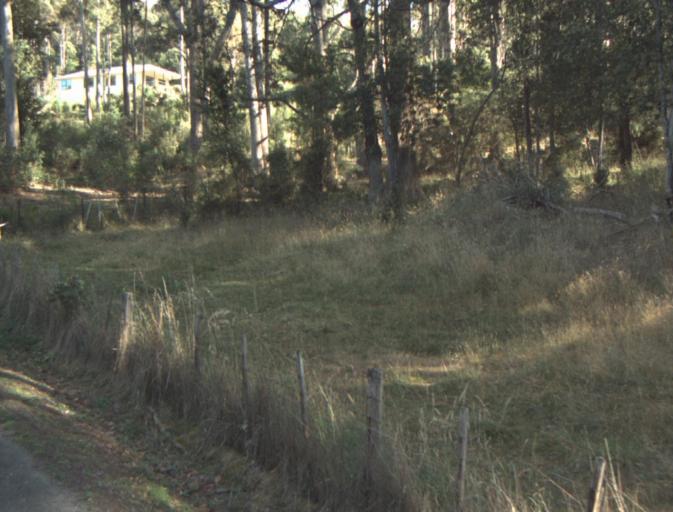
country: AU
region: Tasmania
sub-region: Launceston
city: Mayfield
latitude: -41.2865
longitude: 147.2058
